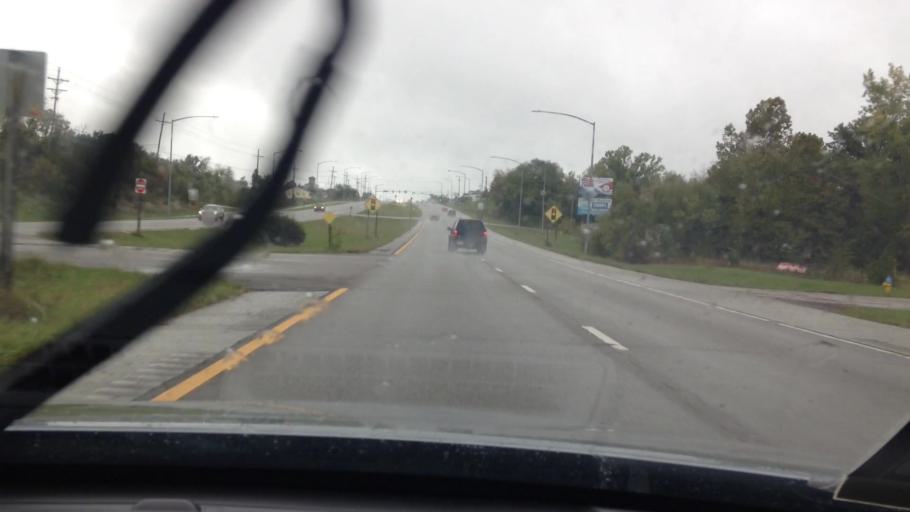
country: US
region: Kansas
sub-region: Leavenworth County
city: Lansing
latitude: 39.2328
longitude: -94.9000
